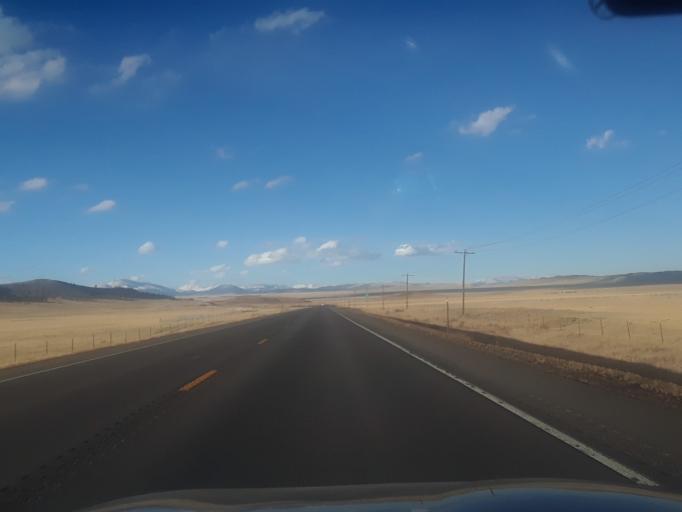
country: US
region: Colorado
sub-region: Chaffee County
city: Buena Vista
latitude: 38.9646
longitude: -105.9600
